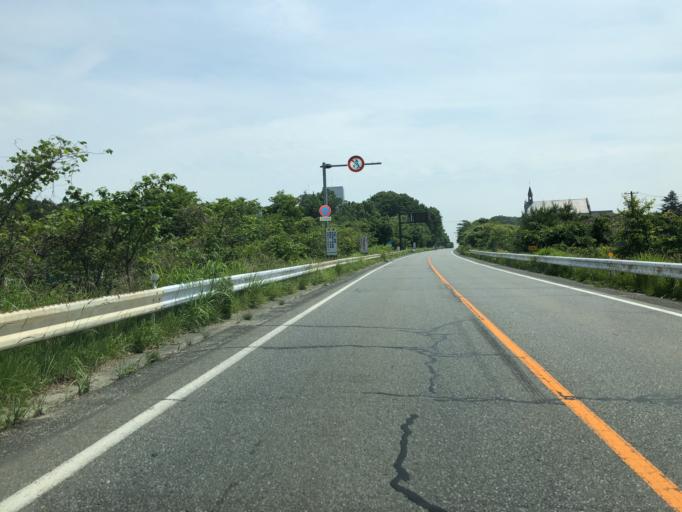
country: JP
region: Fukushima
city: Namie
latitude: 37.4807
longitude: 141.0069
